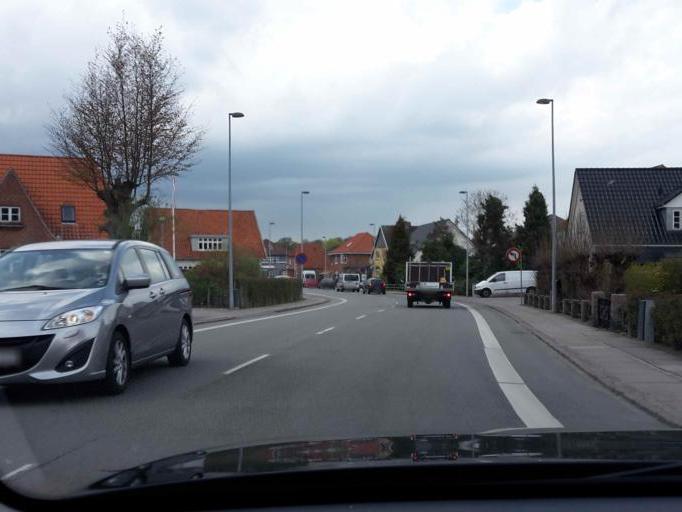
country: DK
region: South Denmark
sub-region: Odense Kommune
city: Odense
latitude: 55.4057
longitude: 10.3523
